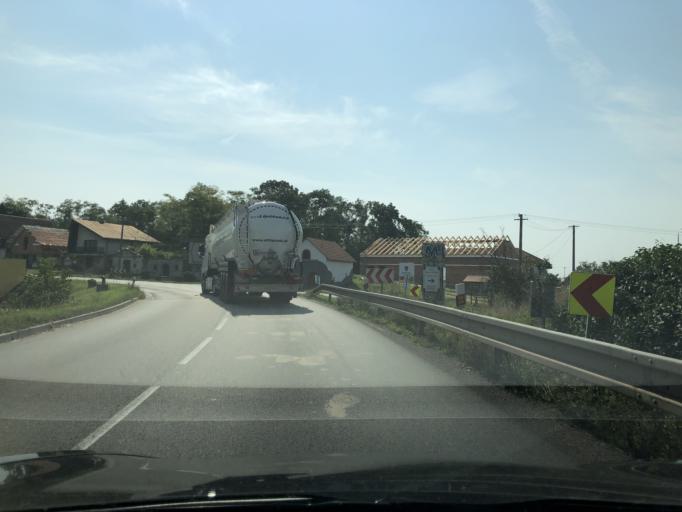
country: CZ
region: South Moravian
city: Novosedly
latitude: 48.8369
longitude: 16.5057
